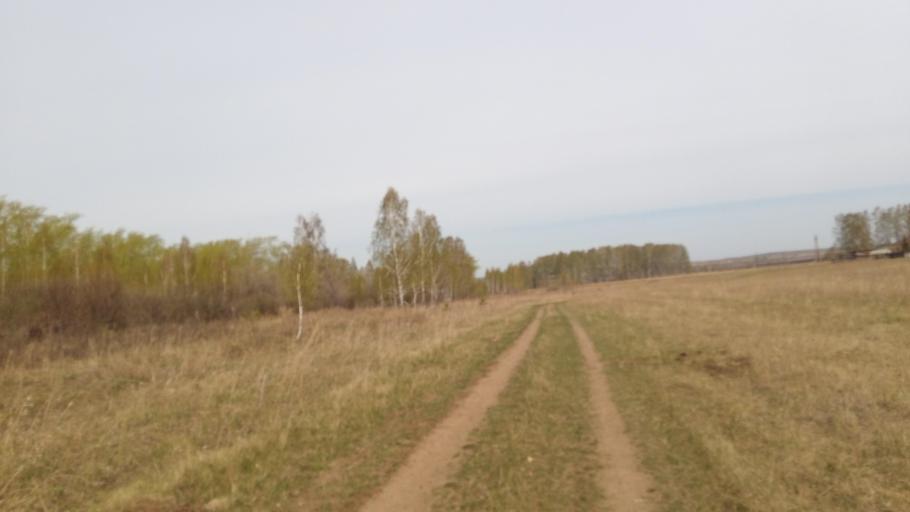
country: RU
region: Chelyabinsk
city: Timiryazevskiy
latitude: 55.0240
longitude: 60.8598
